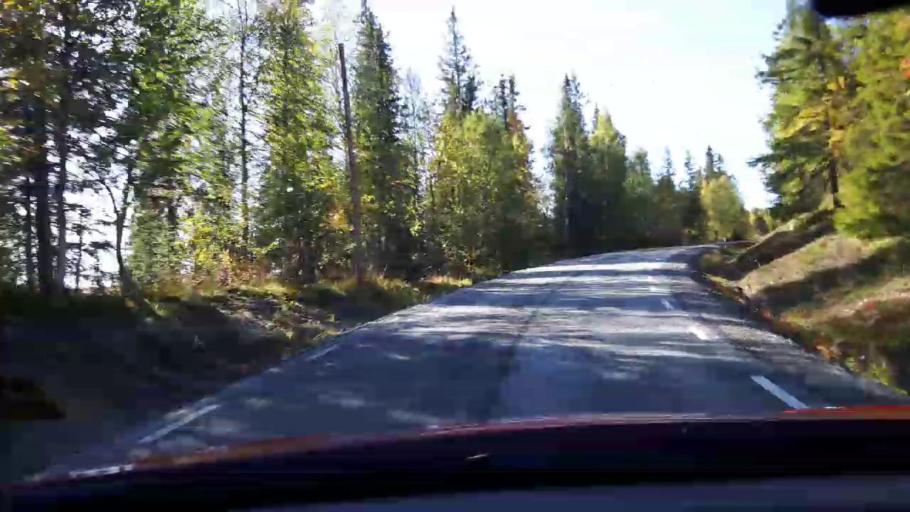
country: NO
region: Nord-Trondelag
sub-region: Royrvik
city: Royrvik
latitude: 64.8168
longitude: 14.2168
